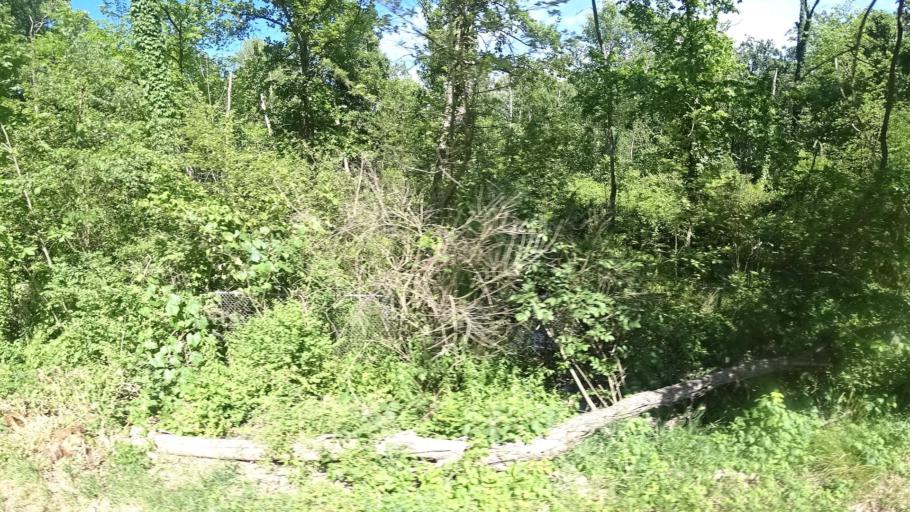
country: US
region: Indiana
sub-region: Porter County
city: Porter
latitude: 41.6522
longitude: -87.0674
